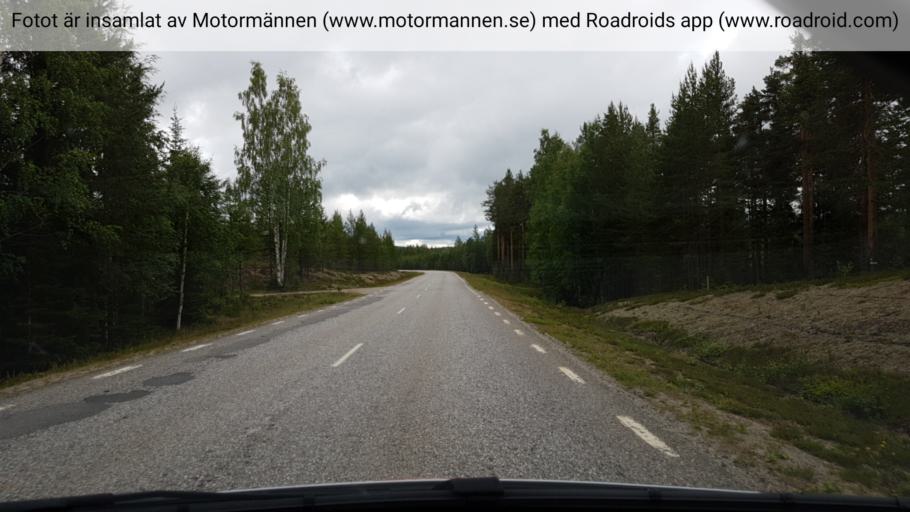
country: SE
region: Vaesterbotten
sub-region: Norsjo Kommun
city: Norsjoe
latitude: 64.6714
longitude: 19.2602
